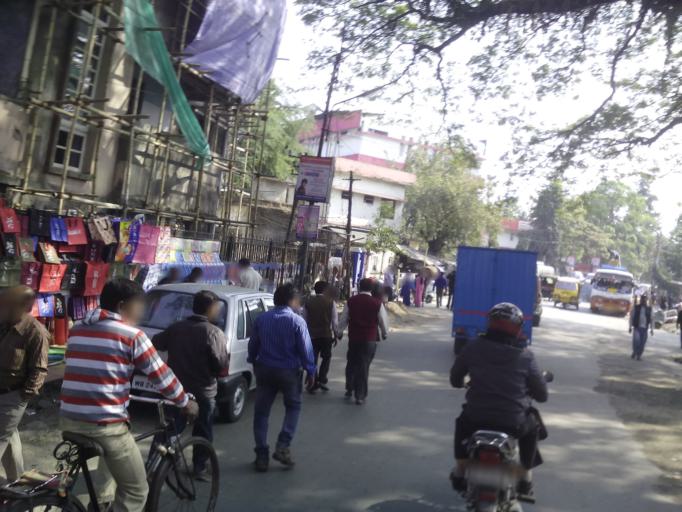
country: IN
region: West Bengal
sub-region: Darjiling
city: Shiliguri
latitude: 26.7101
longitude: 88.4281
